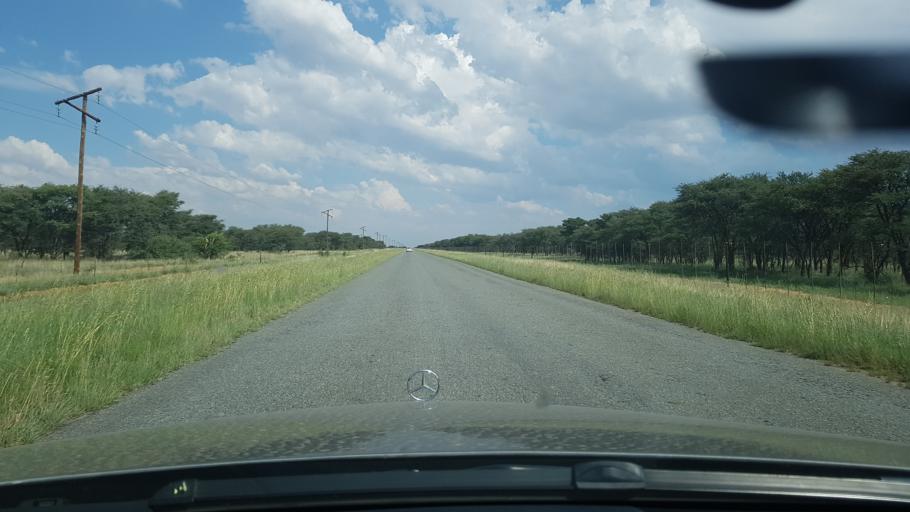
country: ZA
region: North-West
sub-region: Dr Ruth Segomotsi Mompati District Municipality
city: Bloemhof
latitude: -27.7363
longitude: 25.5847
